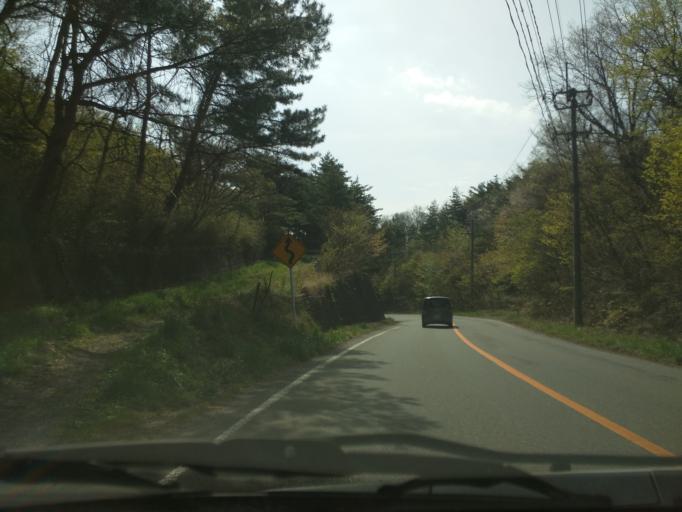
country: JP
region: Fukushima
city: Nihommatsu
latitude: 37.5961
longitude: 140.3644
